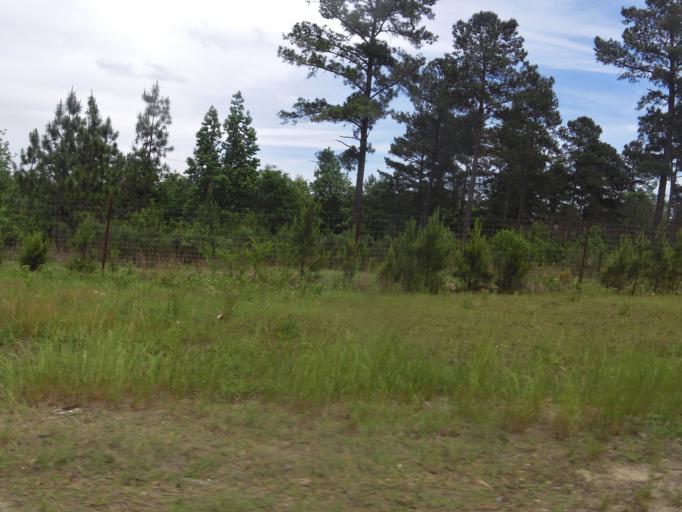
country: US
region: Georgia
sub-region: Candler County
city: Metter
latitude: 32.3841
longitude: -82.1712
